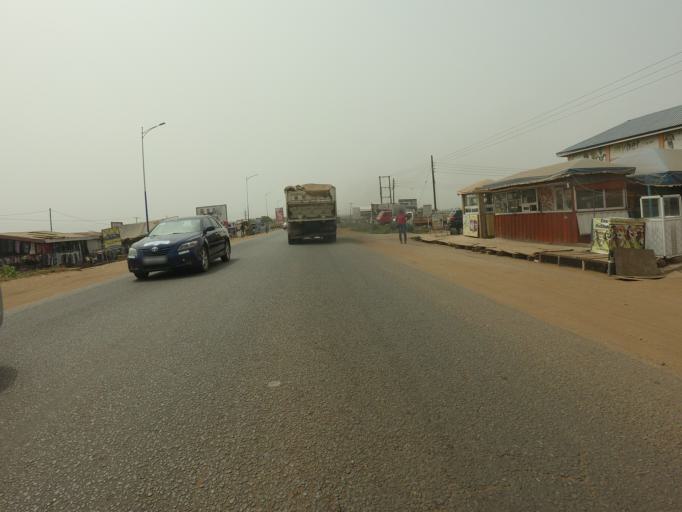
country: GH
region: Greater Accra
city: Tema
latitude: 5.7620
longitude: 0.0530
